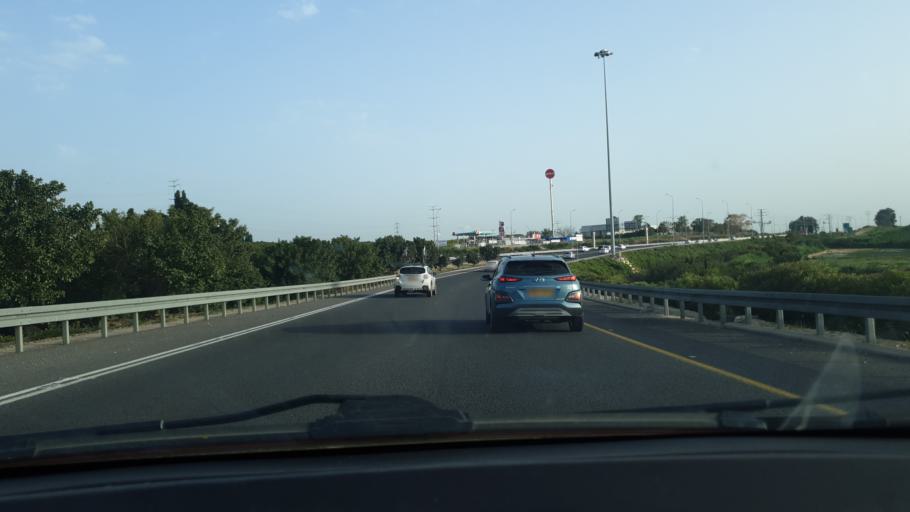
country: IL
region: Central District
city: Even Yehuda
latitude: 32.2536
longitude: 34.8895
